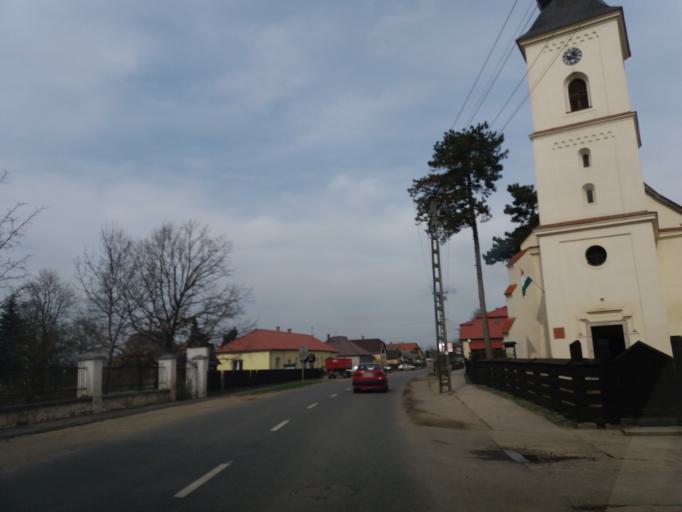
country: HU
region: Szabolcs-Szatmar-Bereg
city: Anarcs
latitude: 48.1738
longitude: 22.0973
